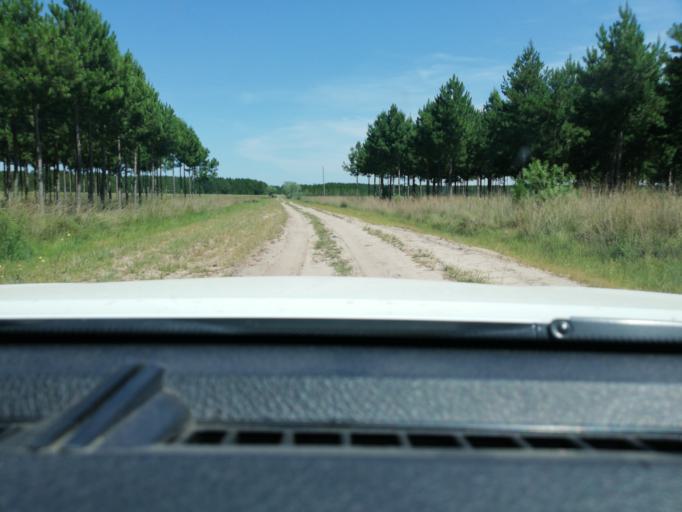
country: AR
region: Corrientes
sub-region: Departamento de San Miguel
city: San Miguel
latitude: -28.0308
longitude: -57.4698
